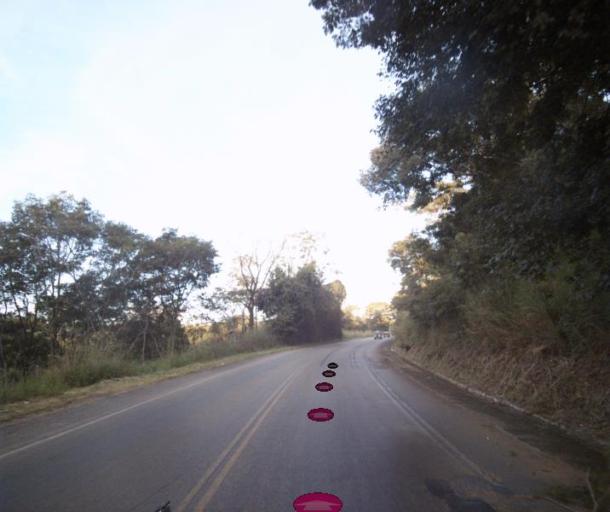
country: BR
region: Goias
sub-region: Abadiania
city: Abadiania
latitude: -16.1108
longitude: -48.8825
